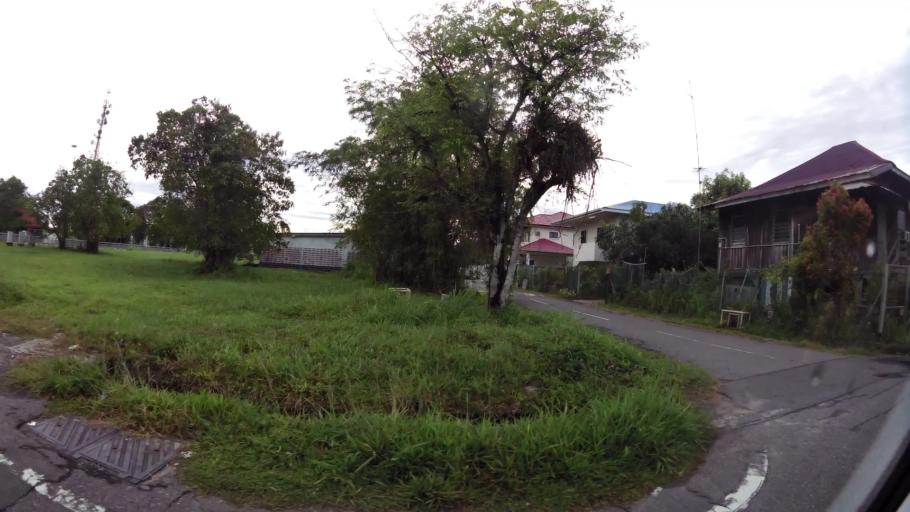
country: BN
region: Belait
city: Seria
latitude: 4.6116
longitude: 114.3311
